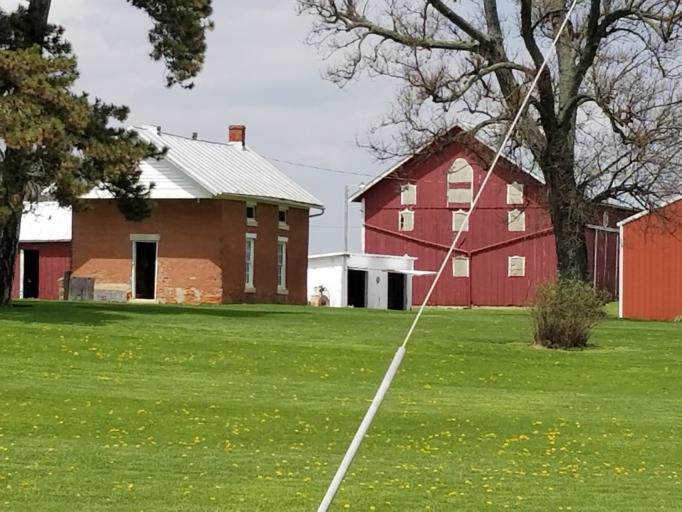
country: US
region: Ohio
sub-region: Wyandot County
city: Upper Sandusky
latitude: 40.9119
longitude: -83.2589
